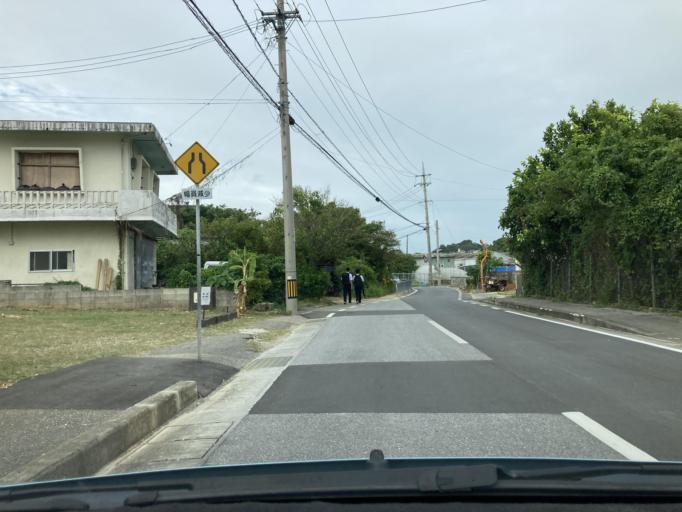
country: JP
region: Okinawa
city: Itoman
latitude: 26.1479
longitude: 127.6933
